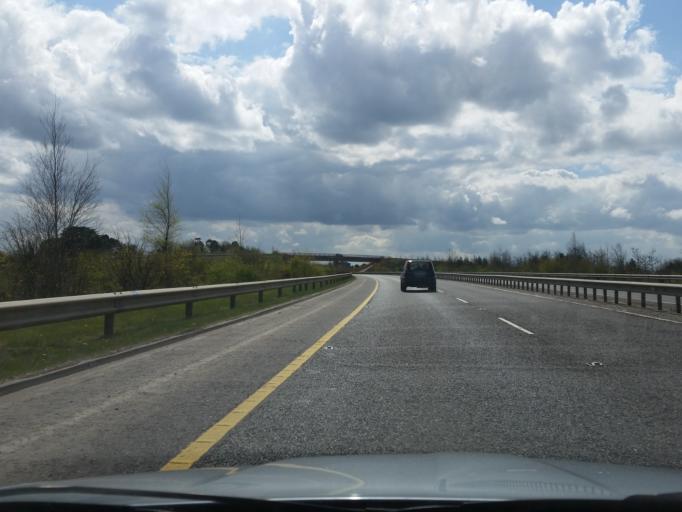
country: IE
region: Leinster
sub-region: An Mhi
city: Ashbourne
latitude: 53.5137
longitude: -6.4206
